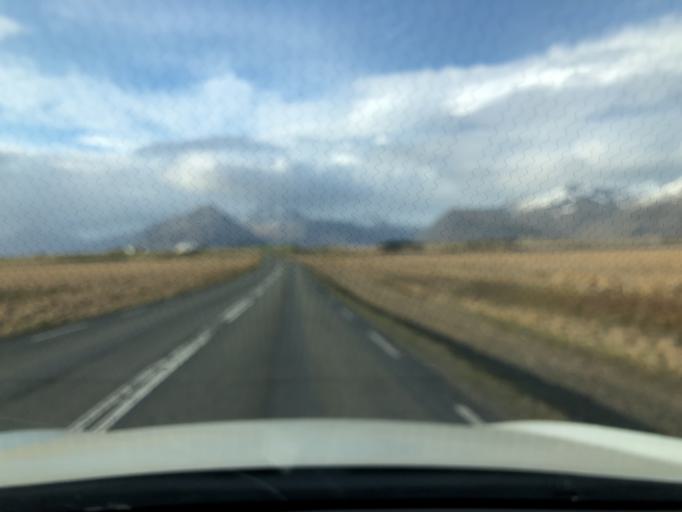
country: IS
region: East
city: Hoefn
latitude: 64.2707
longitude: -15.2023
